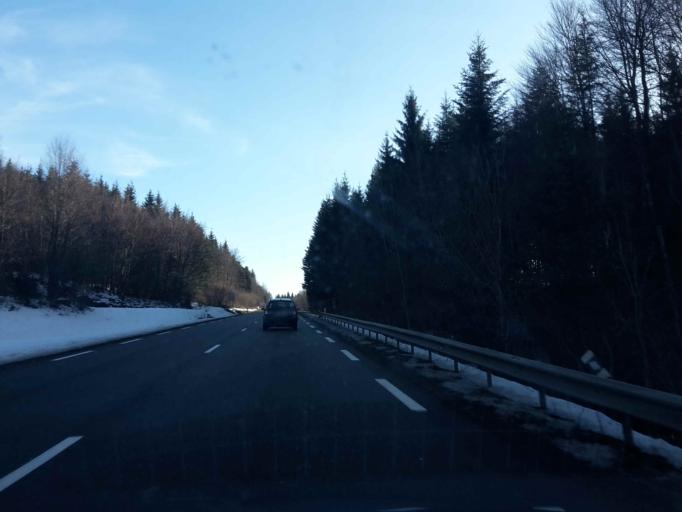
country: FR
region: Franche-Comte
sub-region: Departement du Doubs
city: Doubs
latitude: 47.0078
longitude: 6.3265
